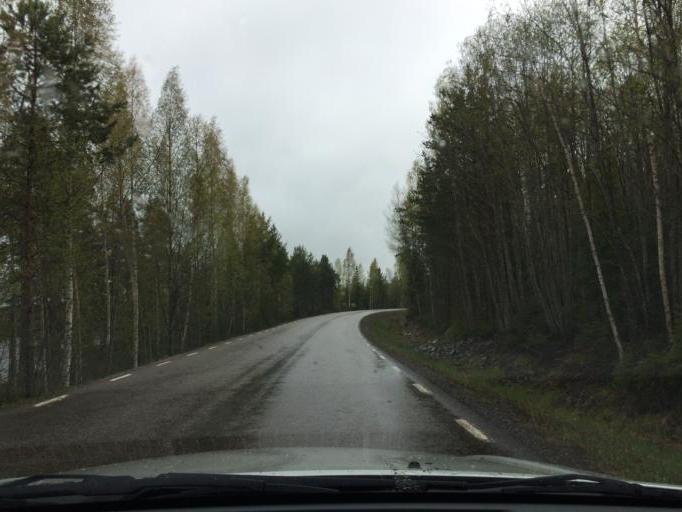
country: SE
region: Dalarna
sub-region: Ludvika Kommun
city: Grangesberg
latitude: 60.0459
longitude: 14.9040
